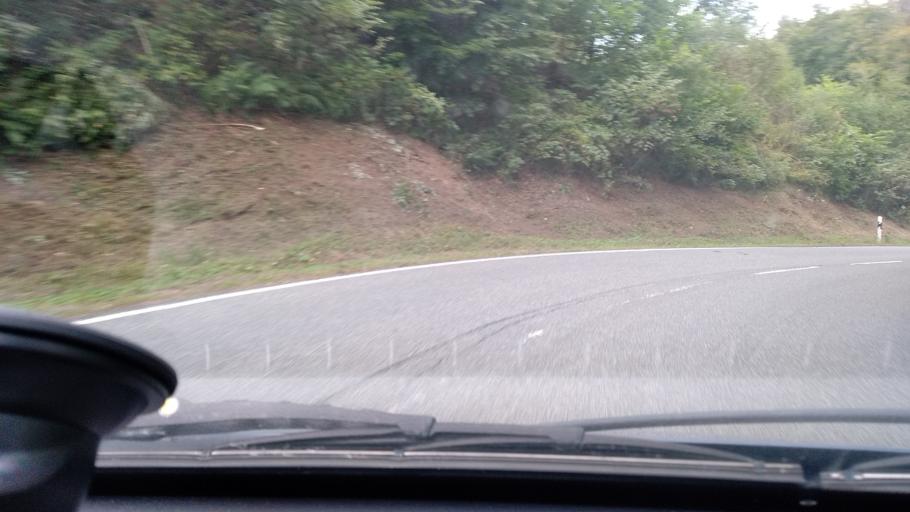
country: DE
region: Hesse
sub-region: Regierungsbezirk Giessen
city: Siegbach
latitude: 50.7910
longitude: 8.3771
